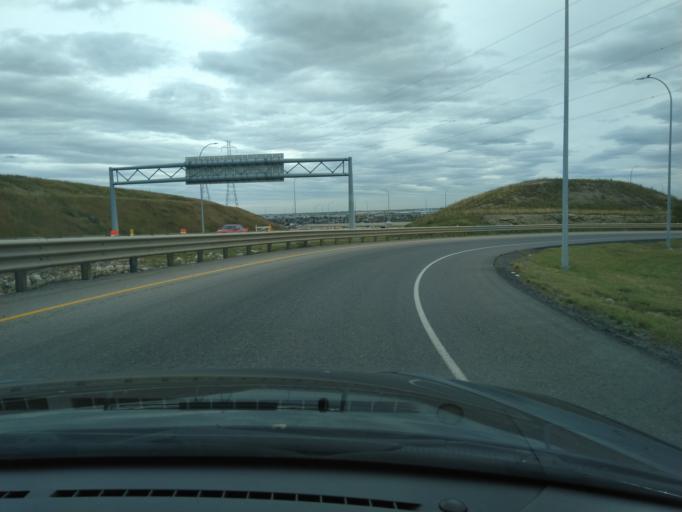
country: CA
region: Alberta
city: Calgary
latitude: 51.1749
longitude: -114.0673
